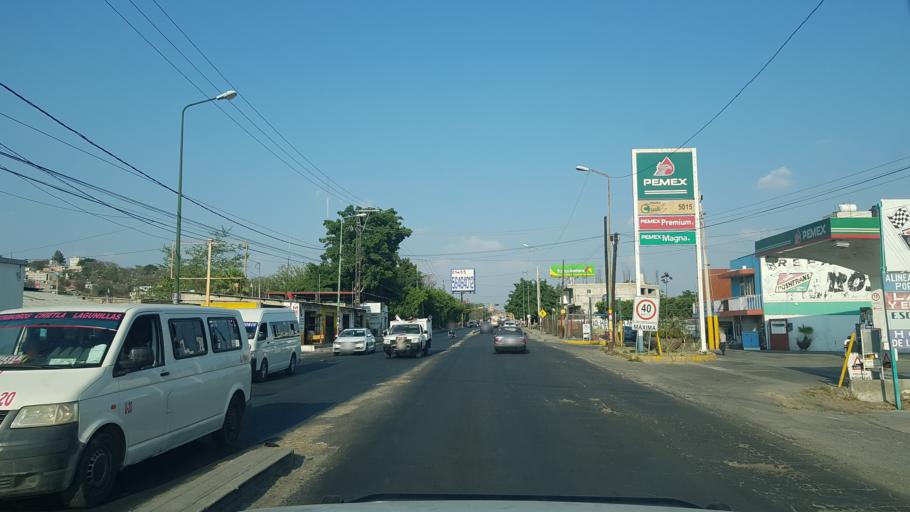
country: MX
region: Puebla
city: Izucar de Matamoros
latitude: 18.6006
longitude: -98.4776
